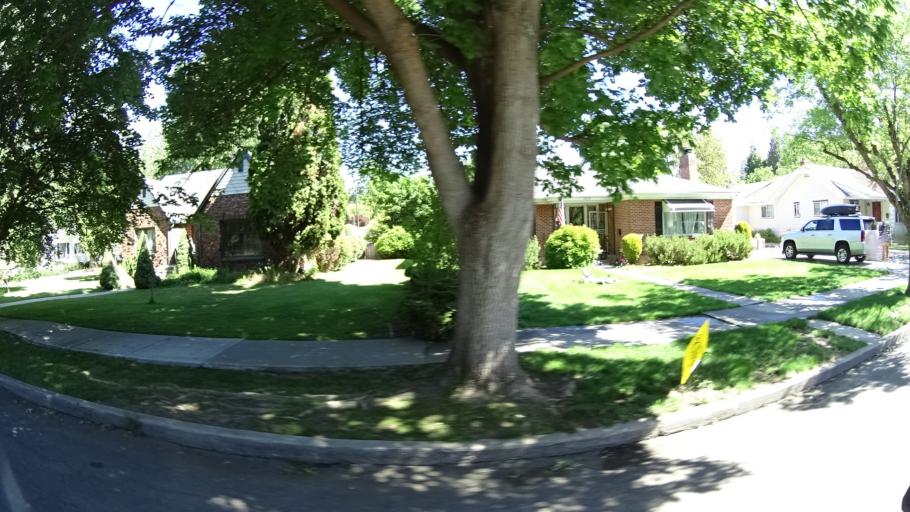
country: US
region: Idaho
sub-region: Ada County
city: Garden City
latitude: 43.6329
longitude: -116.2220
